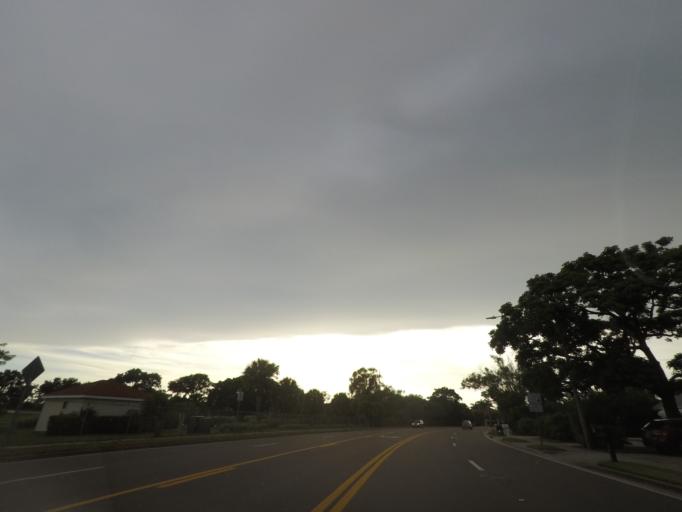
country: US
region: Florida
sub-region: Pinellas County
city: South Pasadena
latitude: 27.7546
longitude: -82.7208
